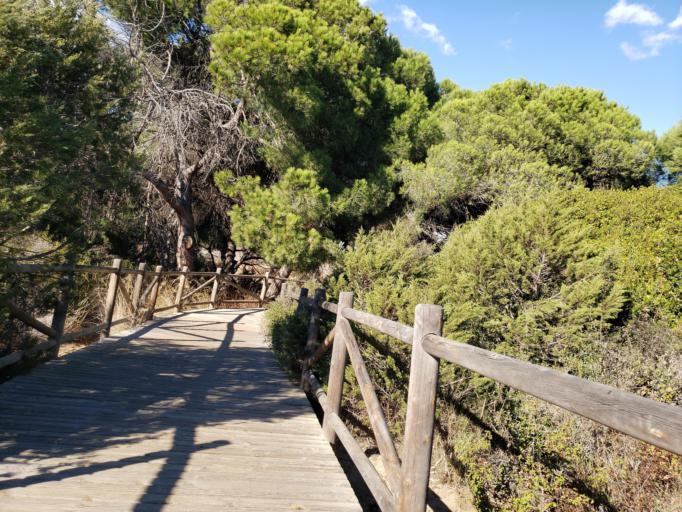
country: ES
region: Andalusia
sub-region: Provincia de Malaga
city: Ojen
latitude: 36.4869
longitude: -4.7491
